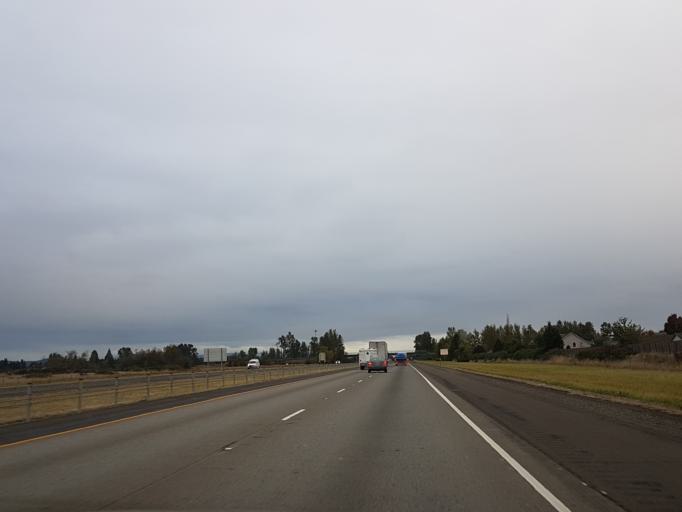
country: US
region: Oregon
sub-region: Linn County
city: Albany
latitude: 44.6166
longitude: -123.0622
